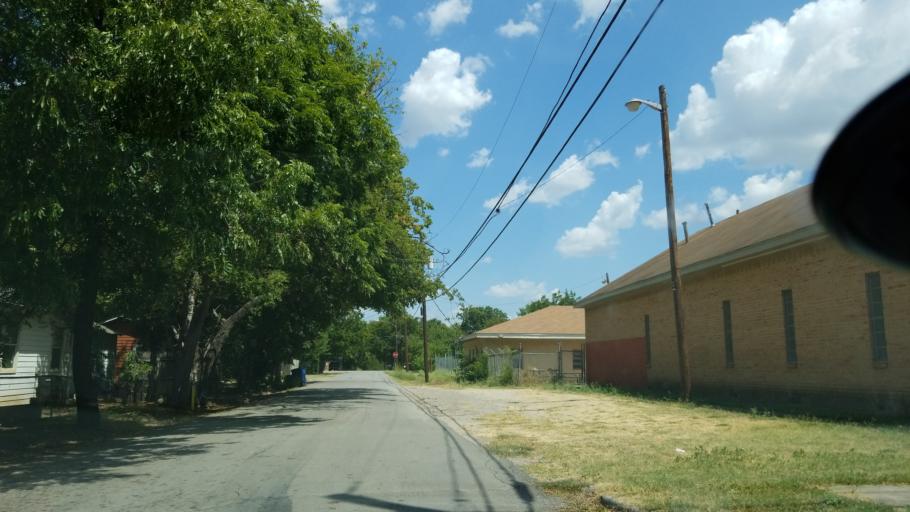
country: US
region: Texas
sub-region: Dallas County
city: Cockrell Hill
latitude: 32.7481
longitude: -96.9088
